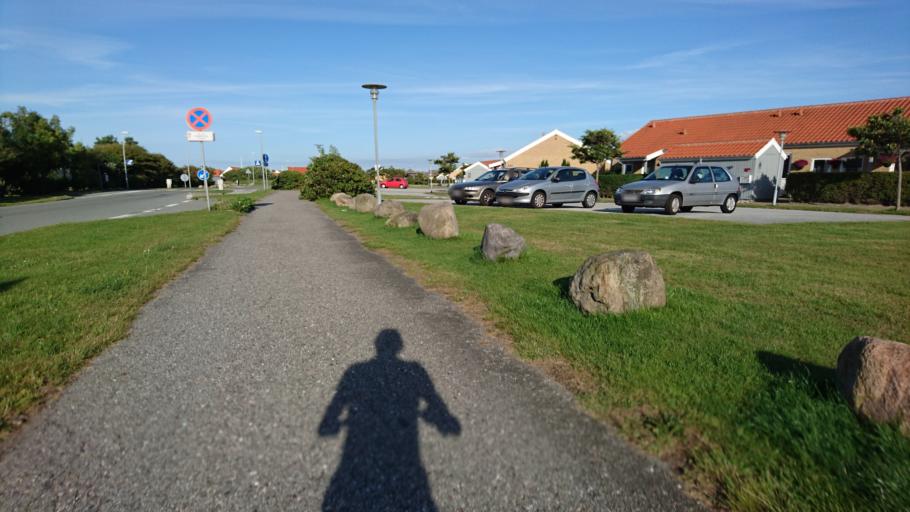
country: DK
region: North Denmark
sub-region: Frederikshavn Kommune
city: Skagen
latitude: 57.7340
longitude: 10.5865
